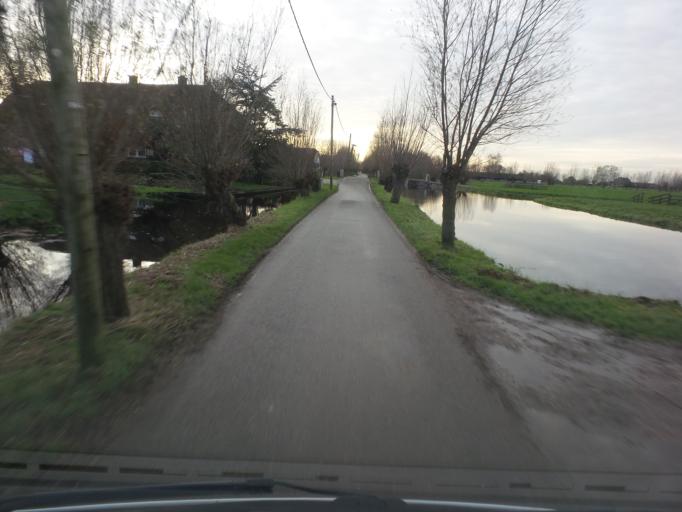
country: NL
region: Utrecht
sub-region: Gemeente Oudewater
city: Oudewater
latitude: 52.0550
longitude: 4.8194
